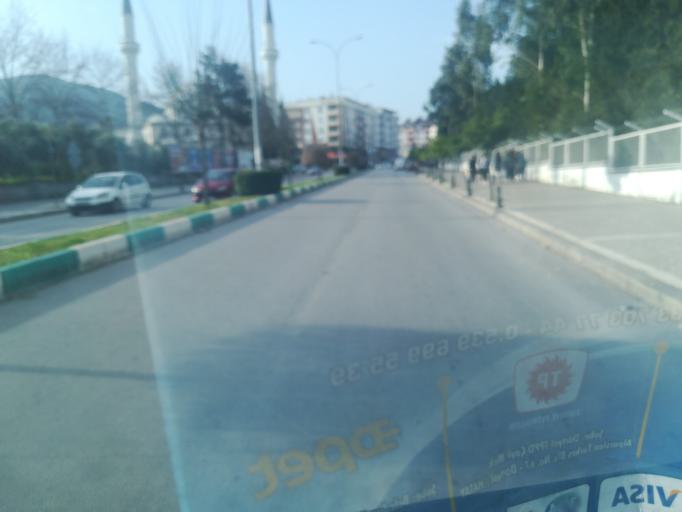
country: TR
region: Osmaniye
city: Osmaniye
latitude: 37.0452
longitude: 36.2261
